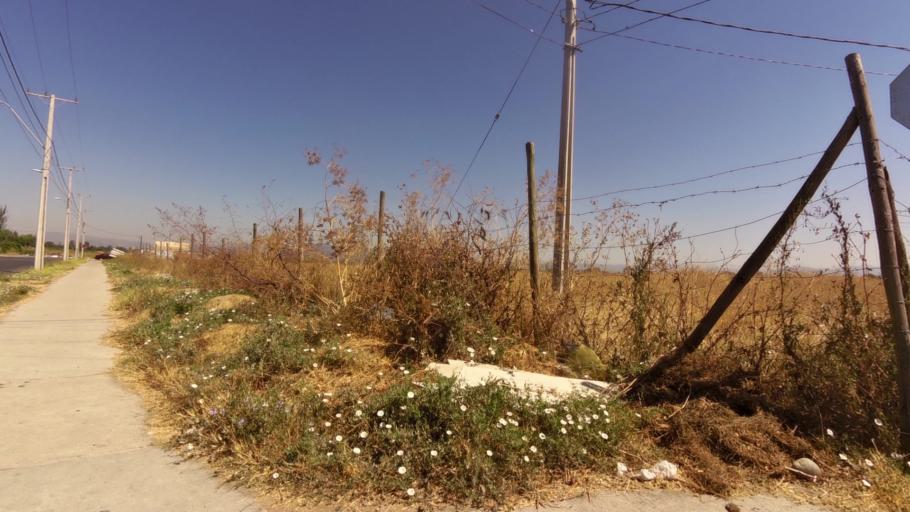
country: CL
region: Maule
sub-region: Provincia de Curico
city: Curico
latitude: -34.9633
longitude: -71.2373
